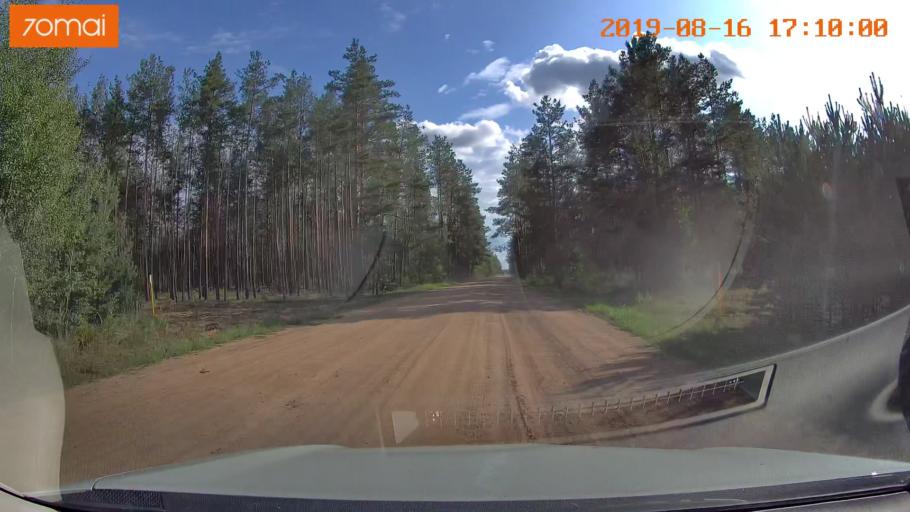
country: BY
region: Mogilev
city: Hlusha
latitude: 53.2059
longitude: 28.9221
